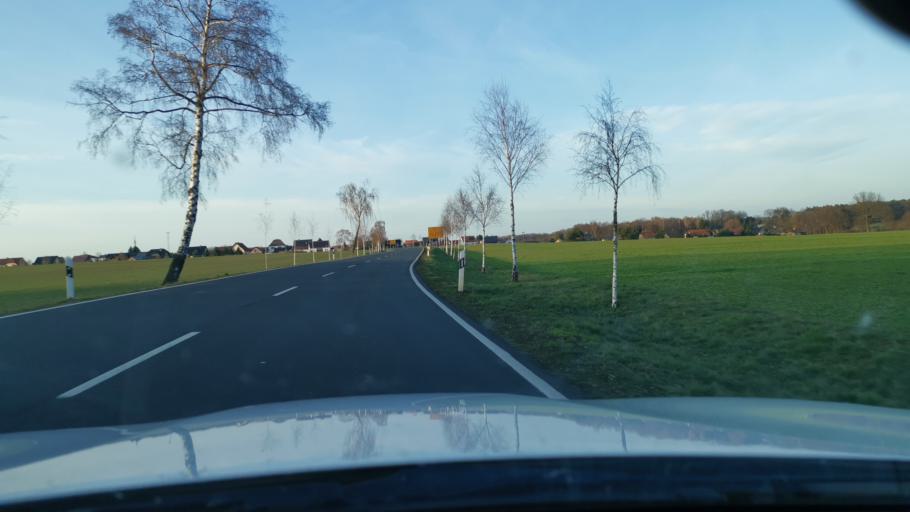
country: DE
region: Saxony
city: Bad Duben
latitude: 51.6304
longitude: 12.5882
